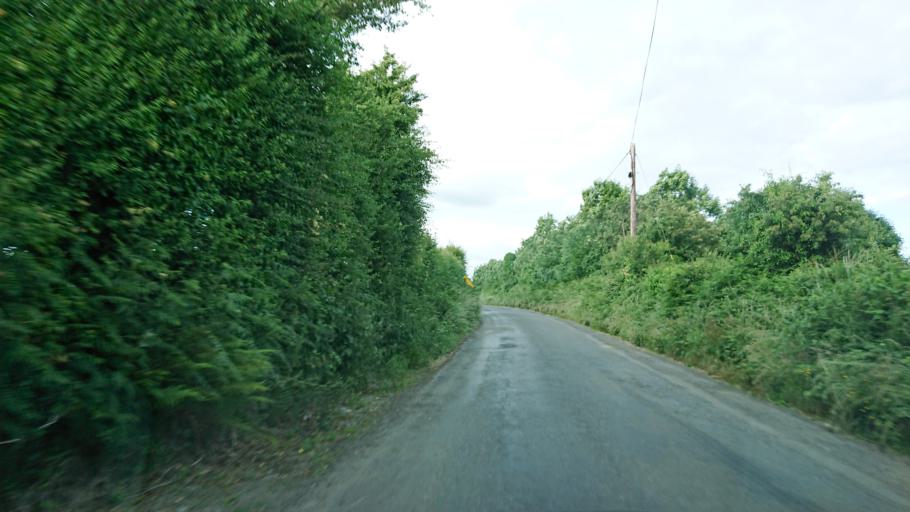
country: IE
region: Munster
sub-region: Waterford
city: Tra Mhor
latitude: 52.2200
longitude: -7.1833
